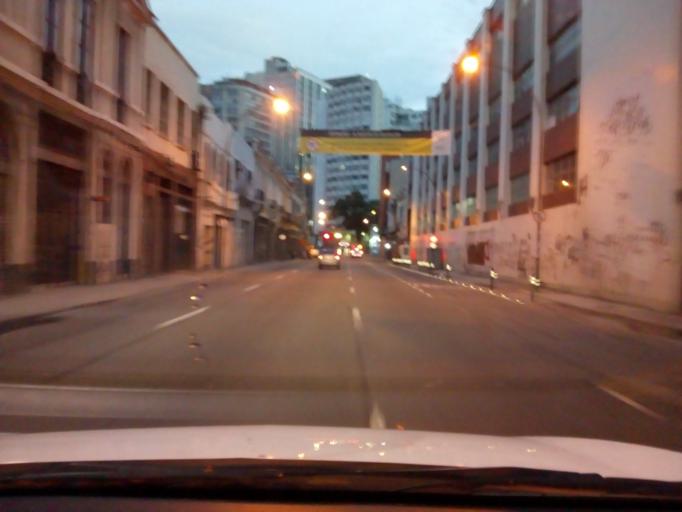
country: BR
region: Rio de Janeiro
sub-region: Rio De Janeiro
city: Rio de Janeiro
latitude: -22.9009
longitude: -43.1861
